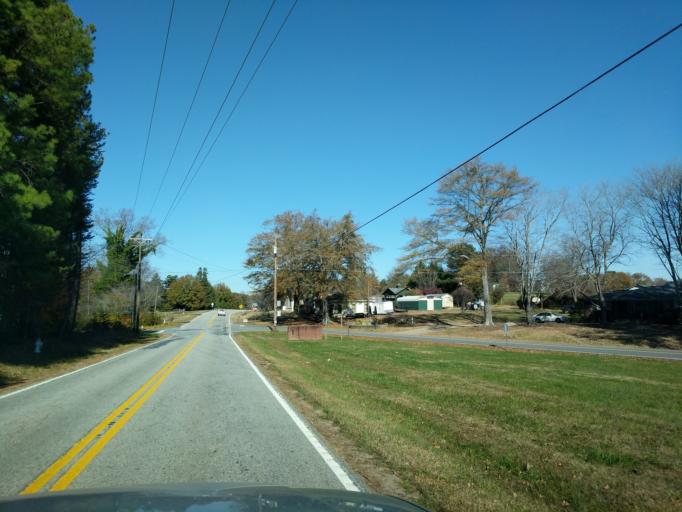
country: US
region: South Carolina
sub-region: Spartanburg County
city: Inman Mills
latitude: 35.0344
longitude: -82.1852
